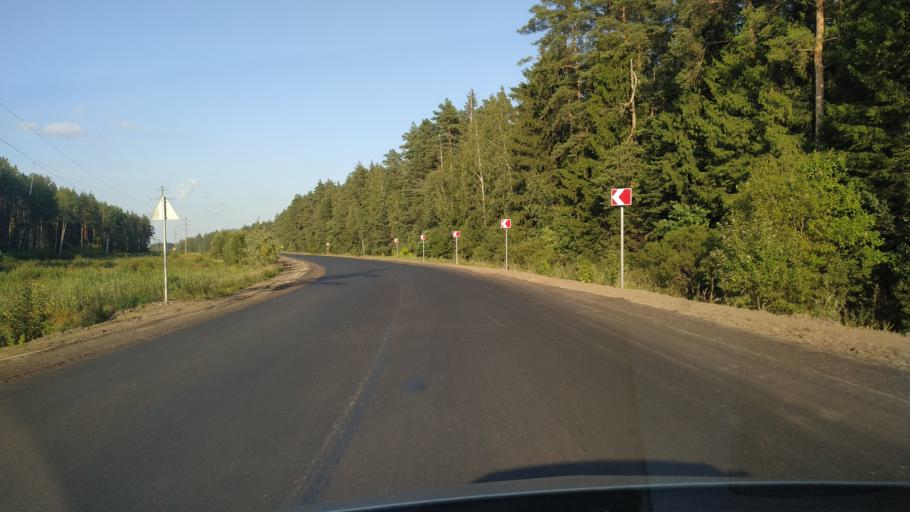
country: RU
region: Moskovskaya
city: Kerva
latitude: 55.5686
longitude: 39.6669
